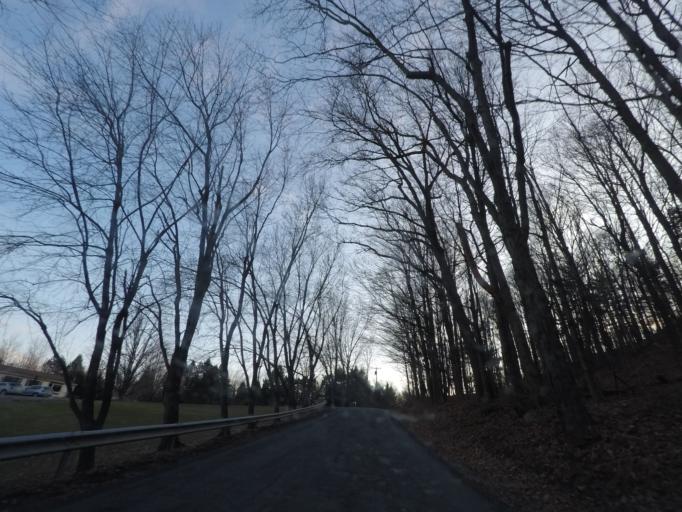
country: US
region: New York
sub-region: Rensselaer County
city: Wynantskill
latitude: 42.6996
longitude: -73.6322
